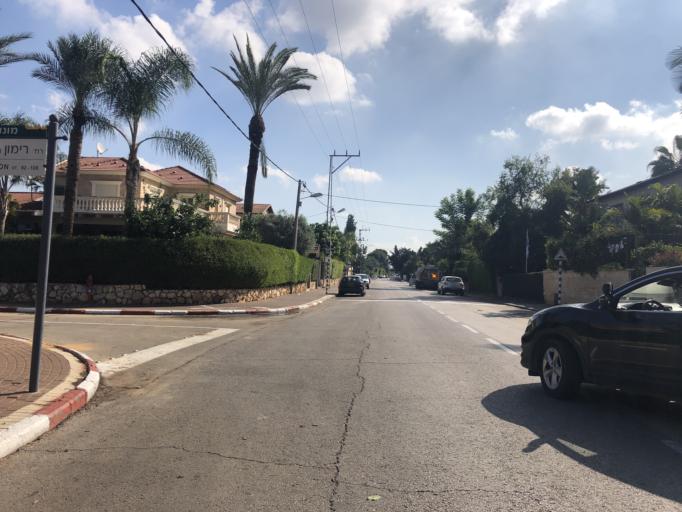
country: IL
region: Central District
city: Yehud
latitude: 32.0297
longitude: 34.8755
